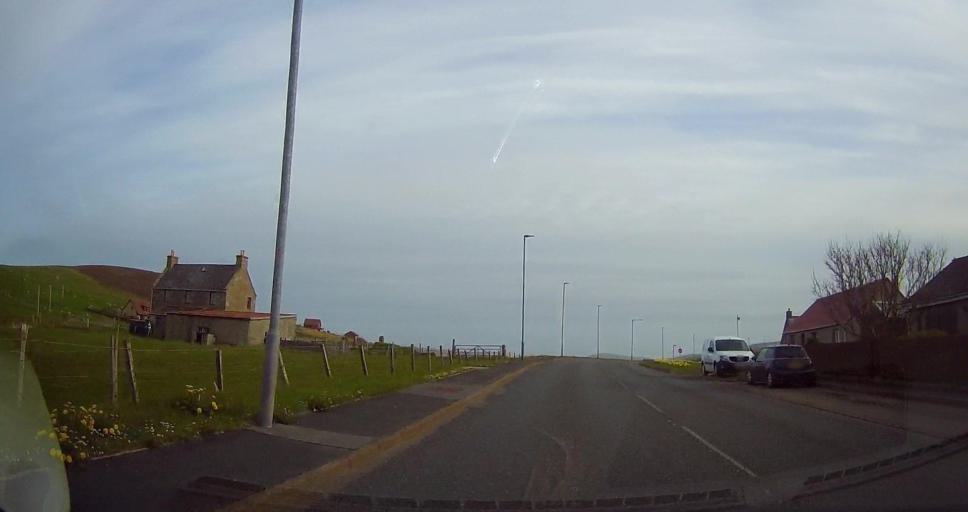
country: GB
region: Scotland
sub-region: Shetland Islands
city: Sandwick
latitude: 60.0547
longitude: -1.2258
